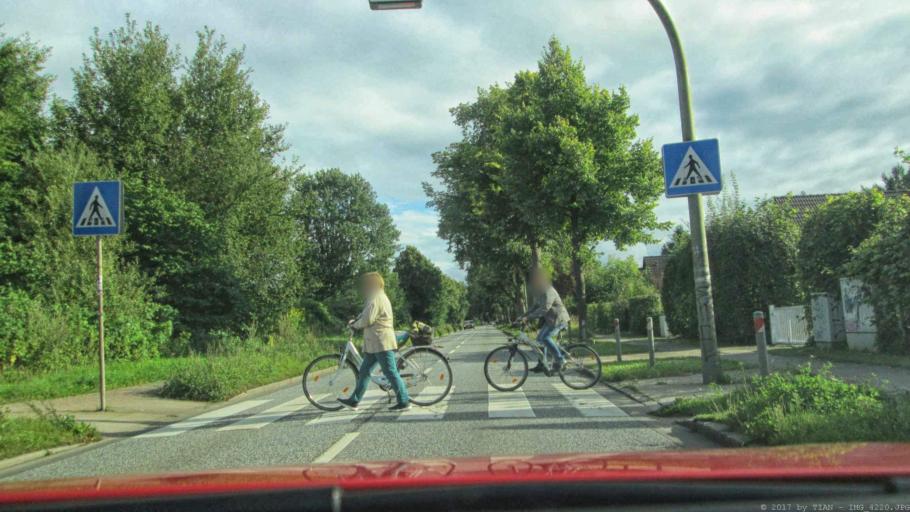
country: DE
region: Schleswig-Holstein
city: Halstenbek
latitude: 53.5810
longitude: 9.8229
